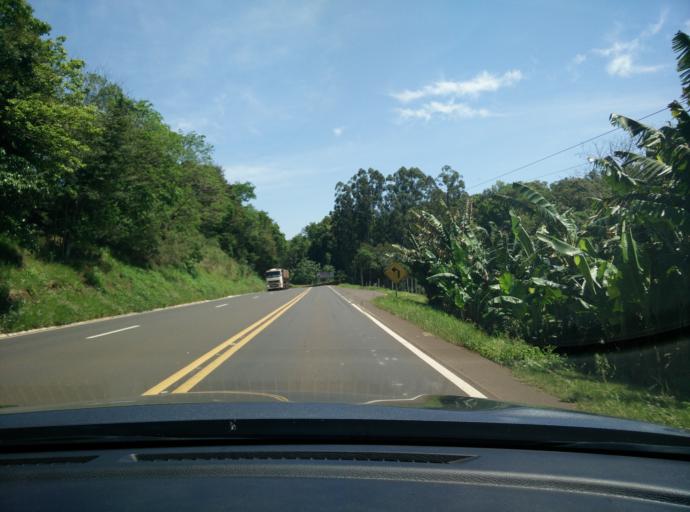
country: BR
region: Parana
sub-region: Santo Antonio Do Sudoeste
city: Santo Antonio do Sudoeste
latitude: -25.8513
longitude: -53.7474
